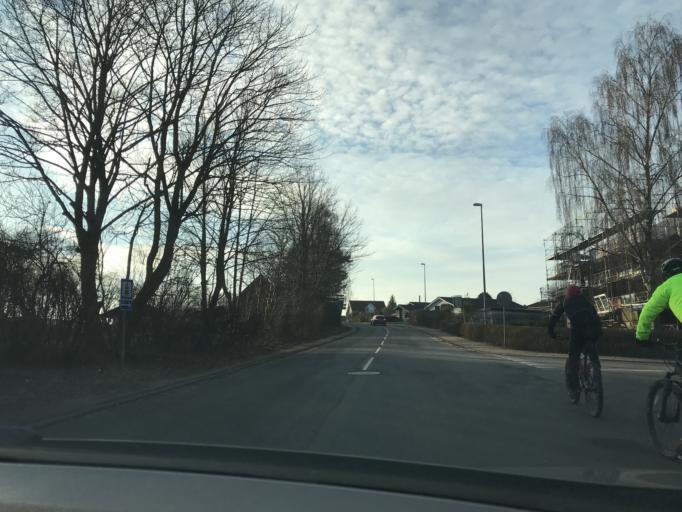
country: DK
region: South Denmark
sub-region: Vejle Kommune
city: Vejle
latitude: 55.7154
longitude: 9.5647
